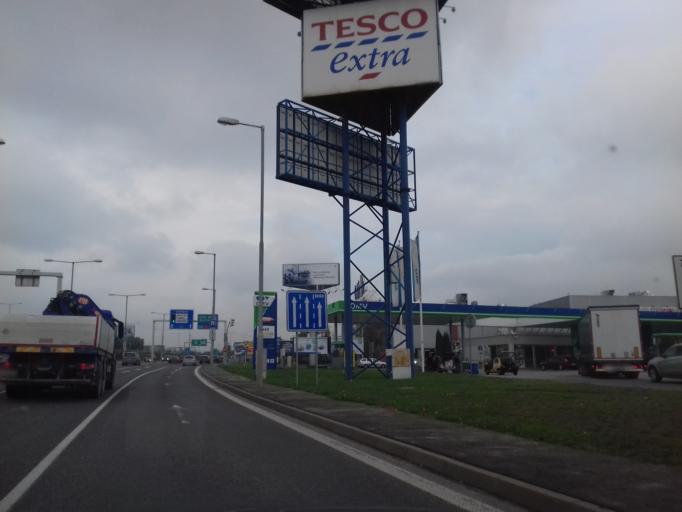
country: SK
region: Bratislavsky
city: Bratislava
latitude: 48.1753
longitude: 17.0650
